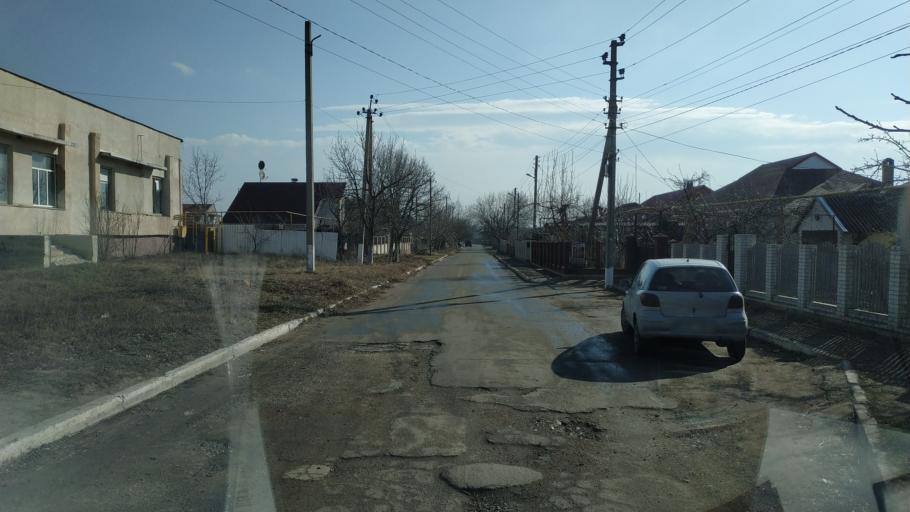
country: MD
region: Chisinau
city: Singera
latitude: 46.6843
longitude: 29.0584
